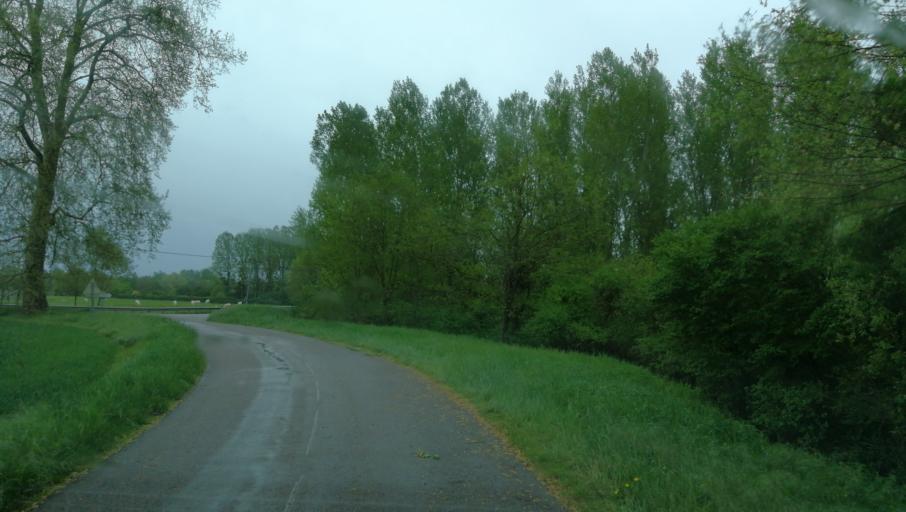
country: FR
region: Bourgogne
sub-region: Departement de Saone-et-Loire
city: Pierre-de-Bresse
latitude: 46.9334
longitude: 5.2410
